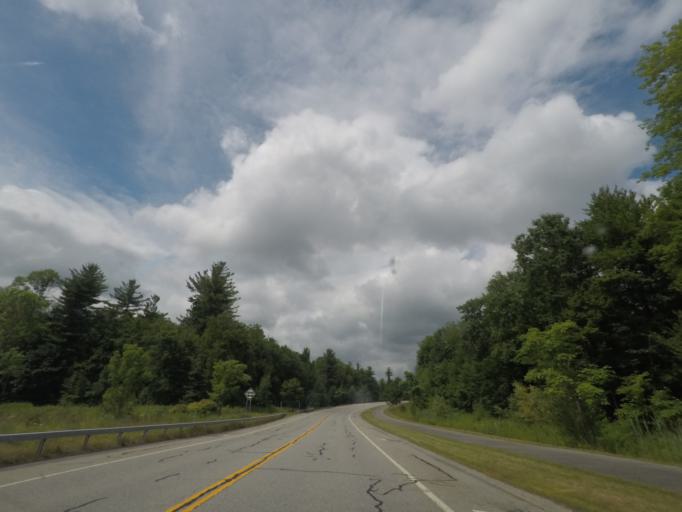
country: US
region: New York
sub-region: Saratoga County
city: Country Knolls
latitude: 42.9556
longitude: -73.7765
